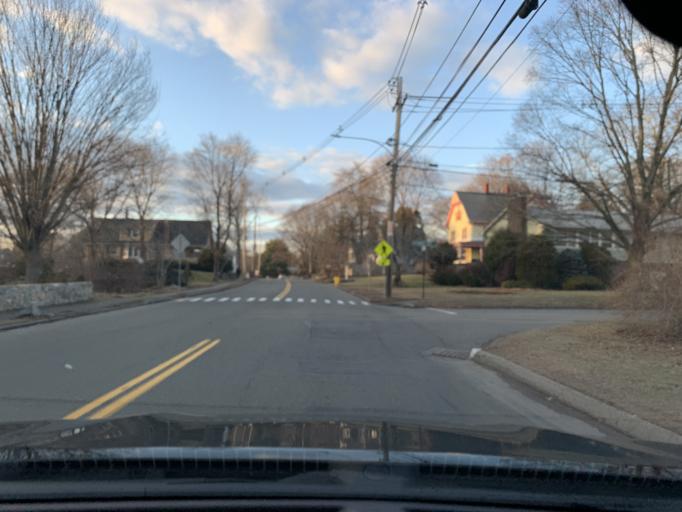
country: US
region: Massachusetts
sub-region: Essex County
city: Lynnfield
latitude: 42.5371
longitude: -71.0452
